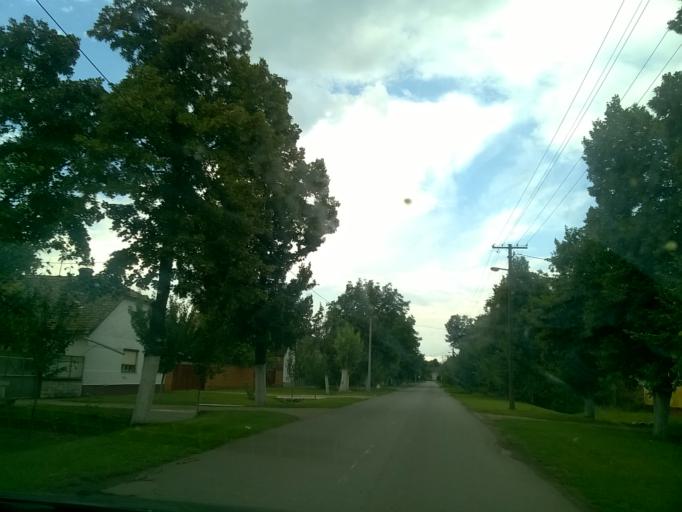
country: RS
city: Tomasevac
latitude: 45.2716
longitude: 20.6243
